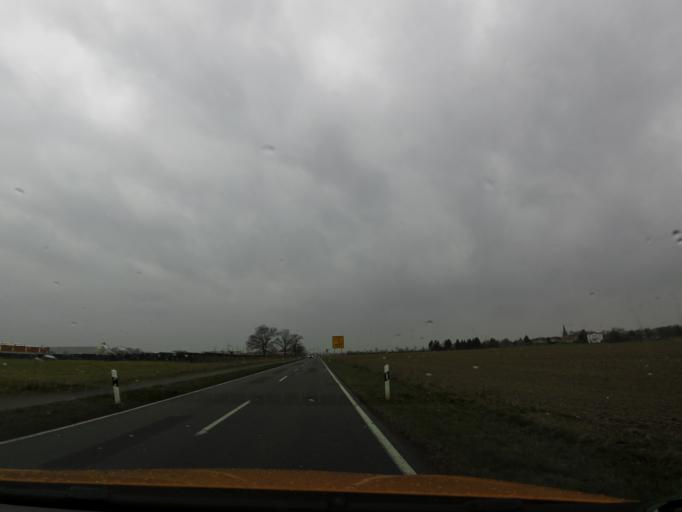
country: DE
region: Brandenburg
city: Brandenburg an der Havel
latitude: 52.4109
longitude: 12.6207
